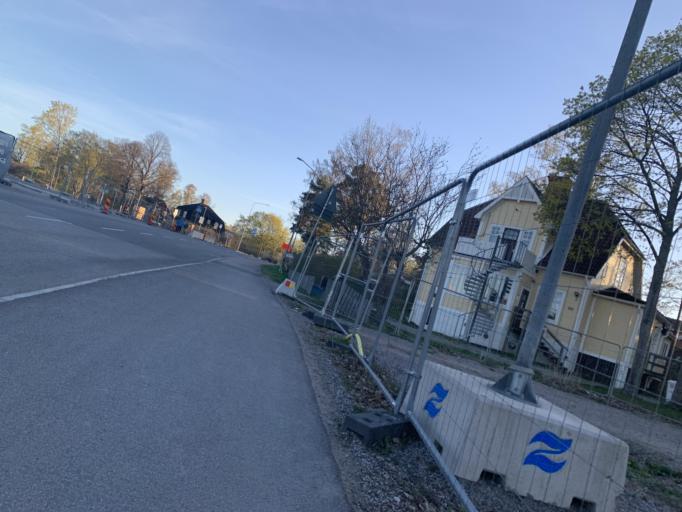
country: SE
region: Stockholm
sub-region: Taby Kommun
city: Taby
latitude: 59.4365
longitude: 18.0535
